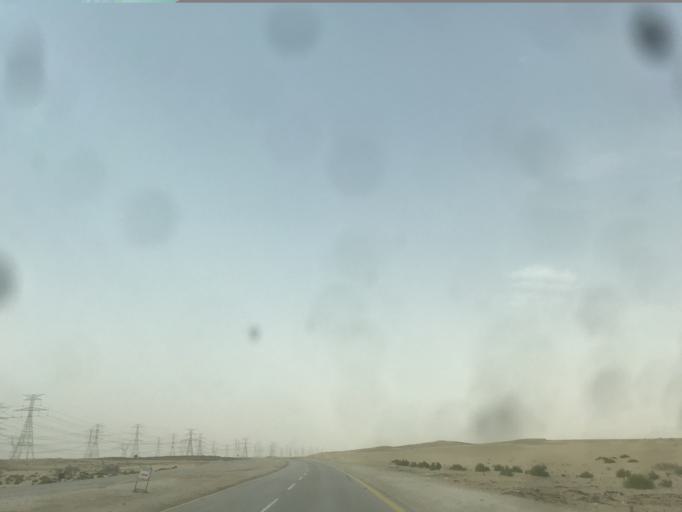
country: SA
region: Eastern Province
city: Abqaiq
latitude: 25.9078
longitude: 49.9004
